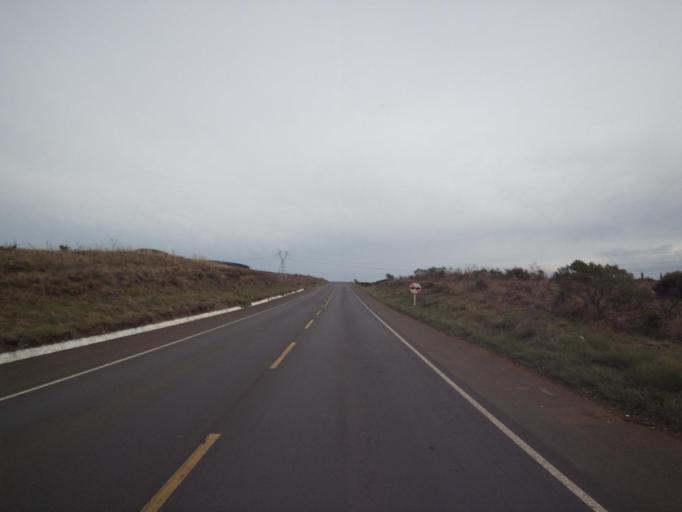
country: BR
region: Parana
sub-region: Palmas
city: Palmas
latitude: -26.6513
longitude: -51.5270
